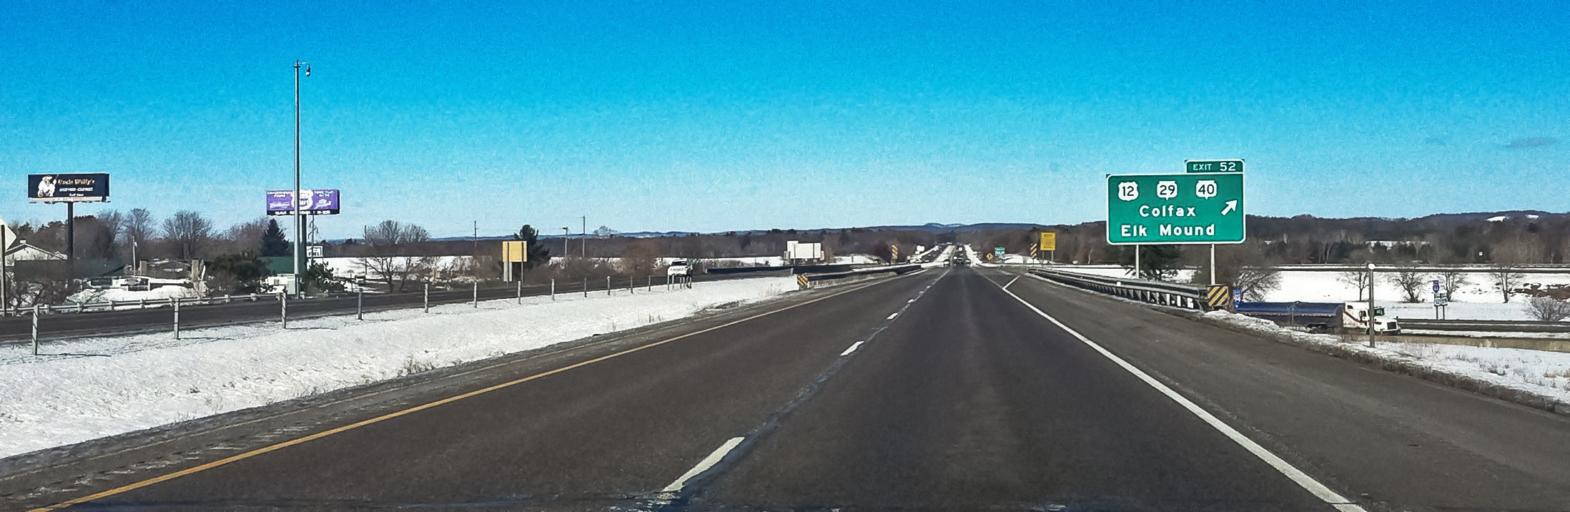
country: US
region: Wisconsin
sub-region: Dunn County
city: Colfax
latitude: 44.8849
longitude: -91.7274
